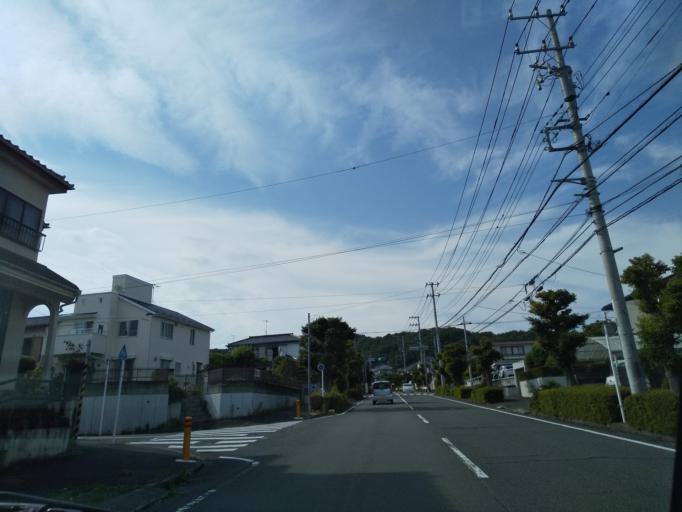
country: JP
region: Kanagawa
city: Zama
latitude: 35.4900
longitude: 139.3353
